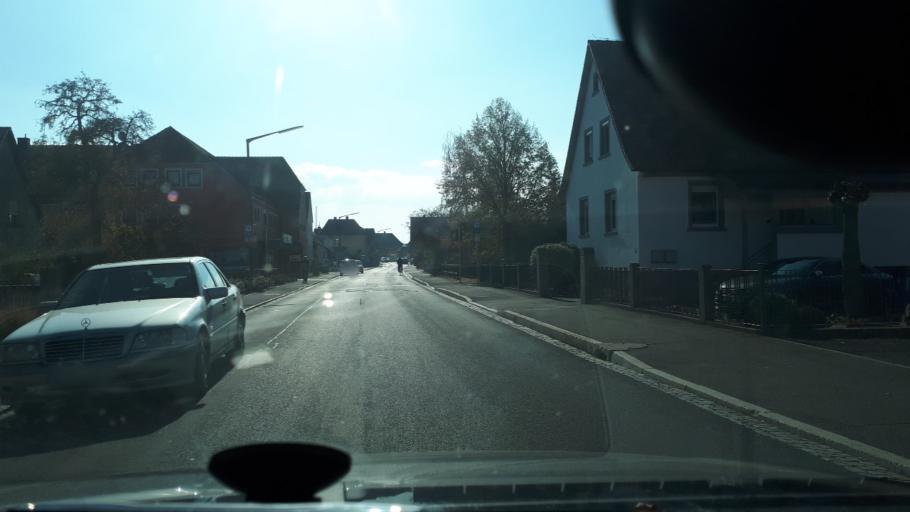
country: DE
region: Bavaria
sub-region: Regierungsbezirk Unterfranken
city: Sommerach
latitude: 49.8024
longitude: 10.2303
